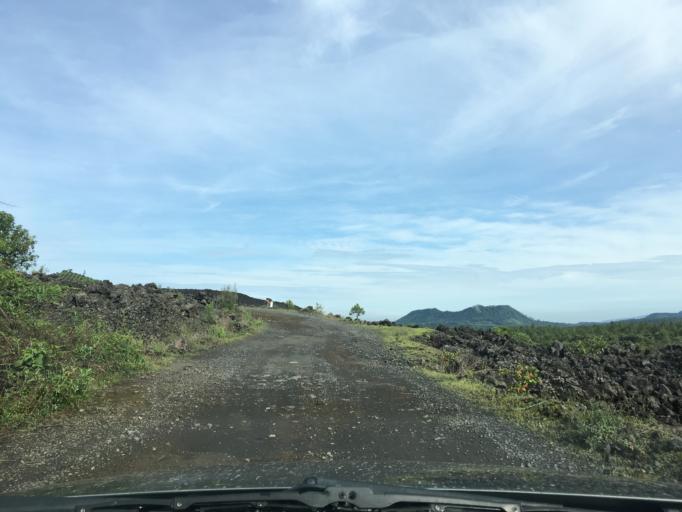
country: MX
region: Michoacan
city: Angahuan
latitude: 19.5223
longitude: -102.2276
